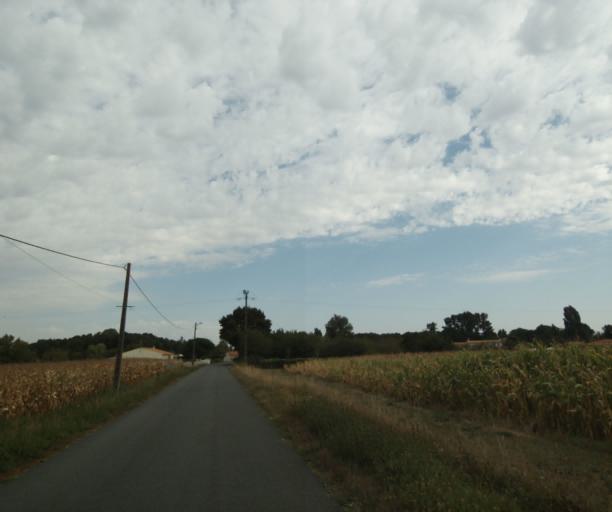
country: FR
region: Poitou-Charentes
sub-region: Departement de la Charente-Maritime
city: Tonnay-Charente
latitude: 45.9617
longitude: -0.8728
